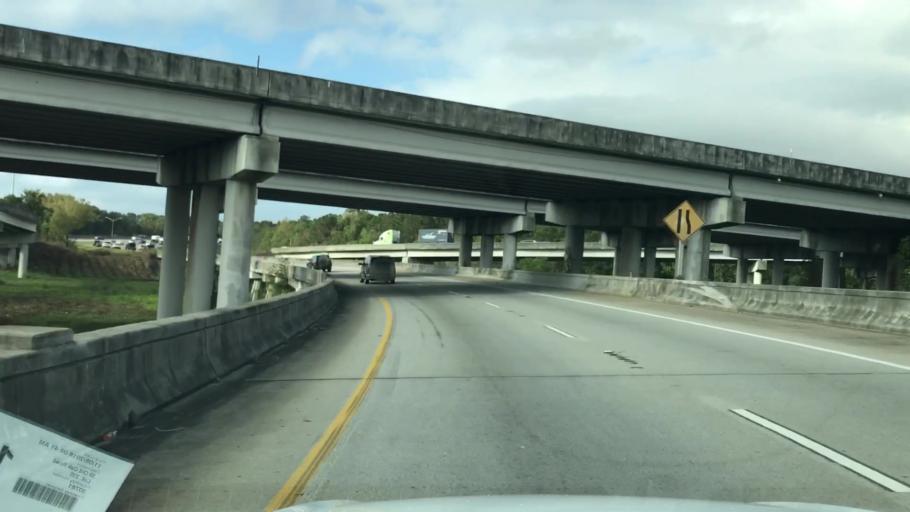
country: US
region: South Carolina
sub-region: Berkeley County
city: Hanahan
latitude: 32.8840
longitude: -80.0177
